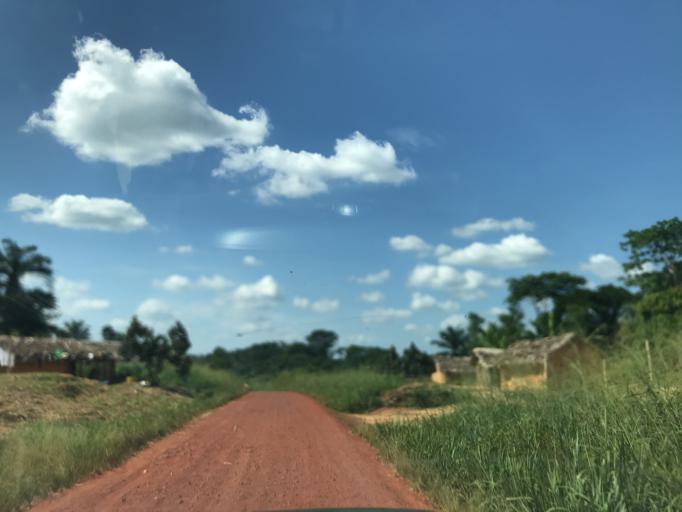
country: CD
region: Eastern Province
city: Kisangani
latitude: 1.2150
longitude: 25.2667
